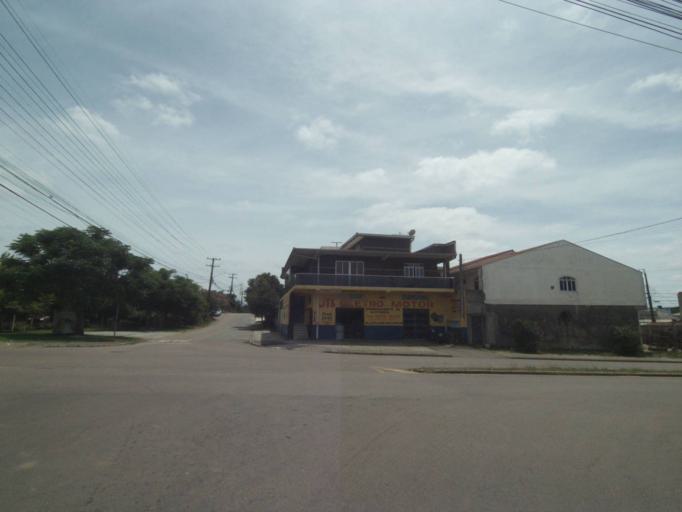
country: BR
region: Parana
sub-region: Curitiba
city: Curitiba
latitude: -25.4952
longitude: -49.3409
